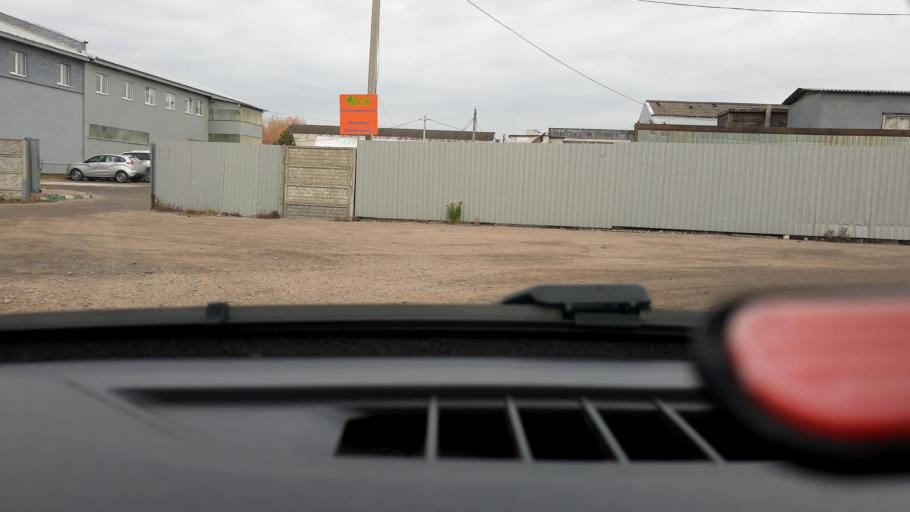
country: RU
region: Nizjnij Novgorod
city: Gorbatovka
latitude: 56.3194
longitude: 43.8466
